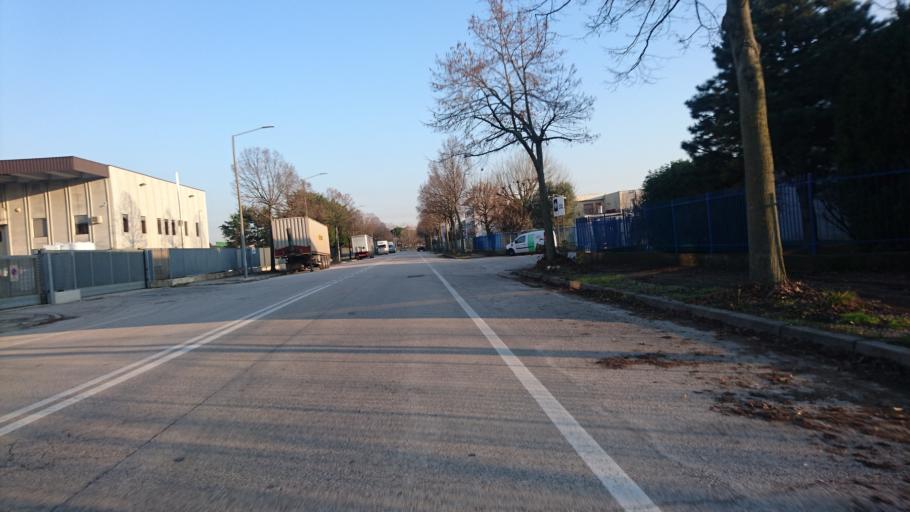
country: IT
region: Veneto
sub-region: Provincia di Padova
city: Villatora
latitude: 45.3943
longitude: 11.9491
